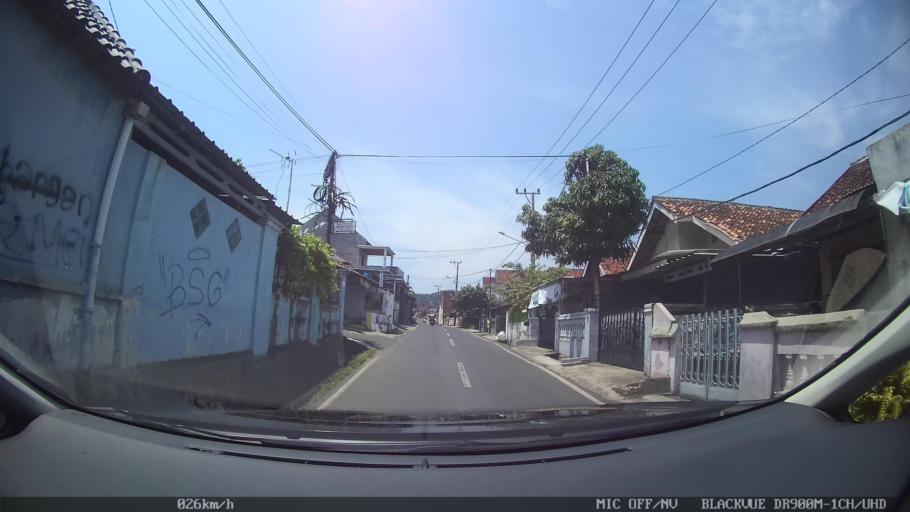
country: ID
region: Lampung
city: Kedaton
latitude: -5.4004
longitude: 105.2639
